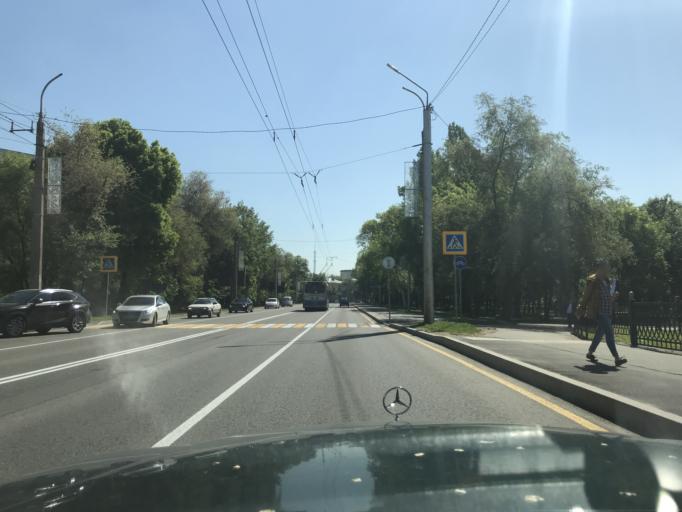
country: KZ
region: Almaty Qalasy
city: Almaty
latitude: 43.2268
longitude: 76.9246
